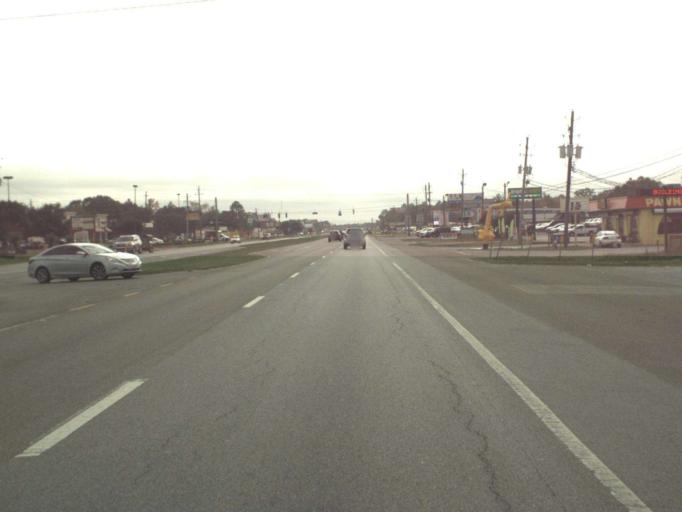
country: US
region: Florida
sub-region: Escambia County
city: Ensley
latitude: 30.5288
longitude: -87.2756
